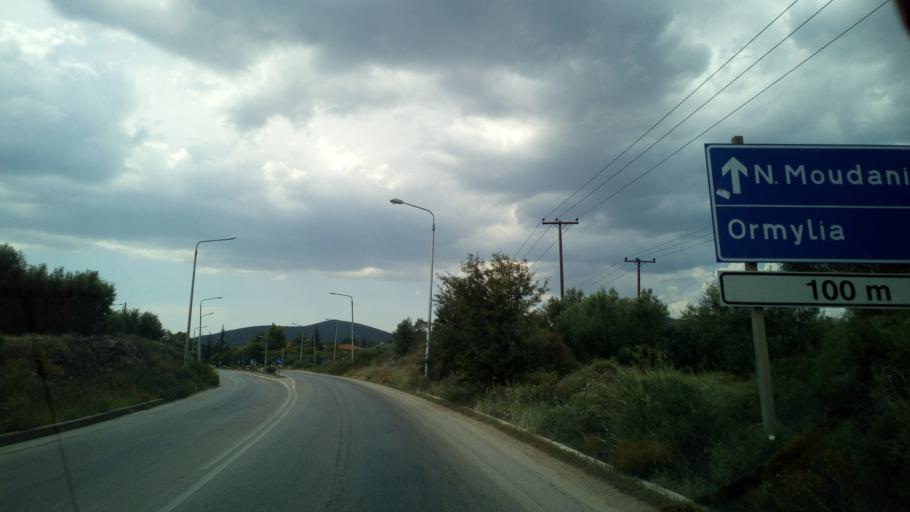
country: GR
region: Central Macedonia
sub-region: Nomos Chalkidikis
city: Ormylia
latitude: 40.2625
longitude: 23.5186
